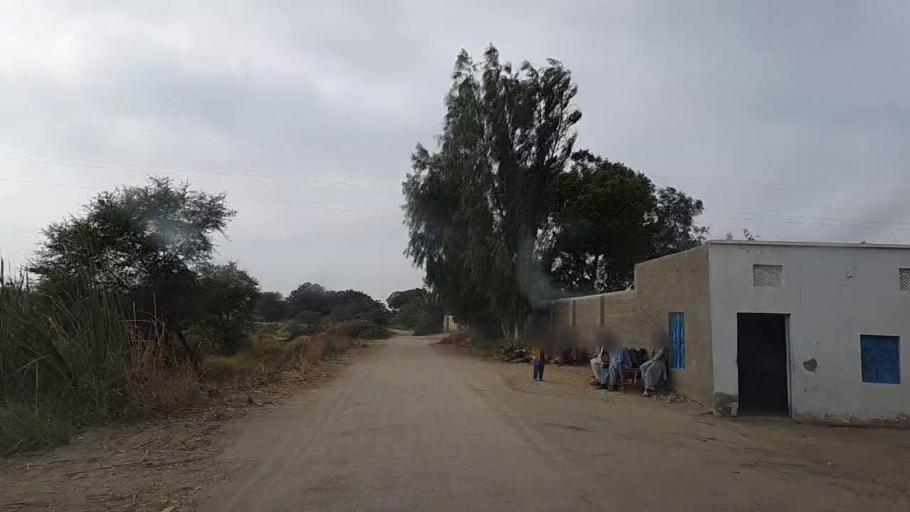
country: PK
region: Sindh
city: Sanghar
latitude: 26.1741
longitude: 68.9528
